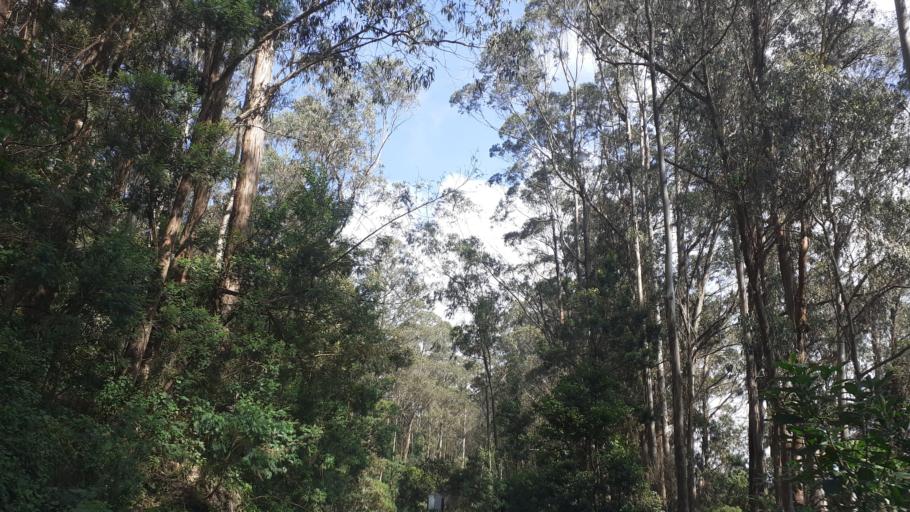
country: IN
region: Tamil Nadu
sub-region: Dindigul
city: Kodaikanal
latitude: 10.2294
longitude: 77.4238
